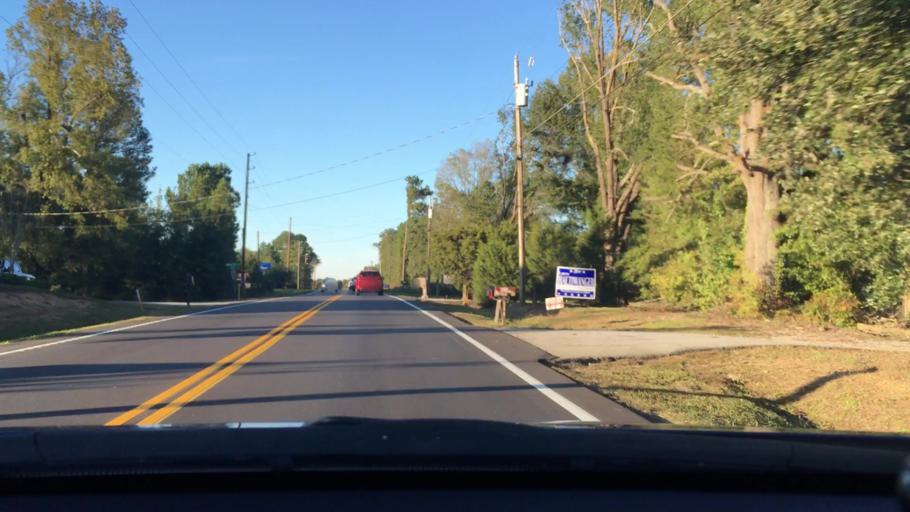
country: US
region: South Carolina
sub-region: Lexington County
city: Irmo
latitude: 34.1002
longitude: -81.1602
